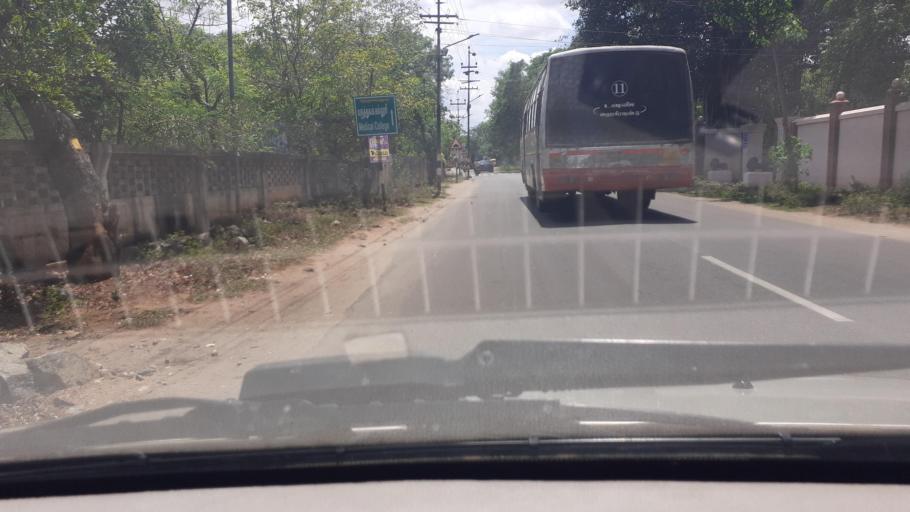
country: IN
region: Tamil Nadu
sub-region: Tirunelveli Kattabo
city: Tirunelveli
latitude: 8.7147
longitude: 77.7504
